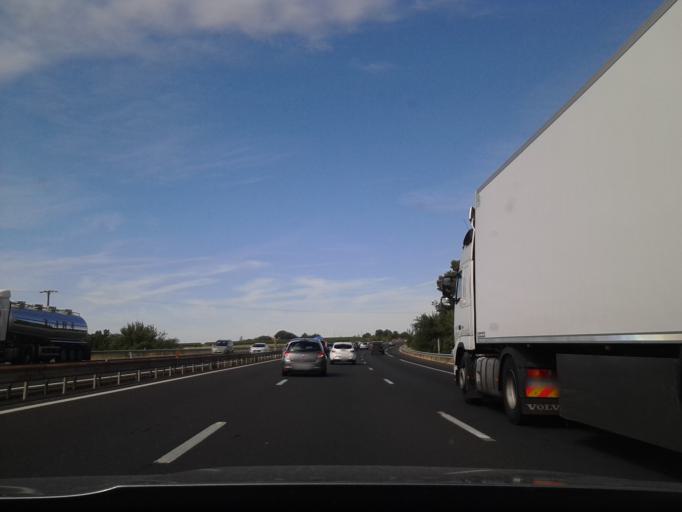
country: FR
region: Languedoc-Roussillon
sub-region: Departement de l'Herault
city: Pinet
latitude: 43.4243
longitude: 3.5509
